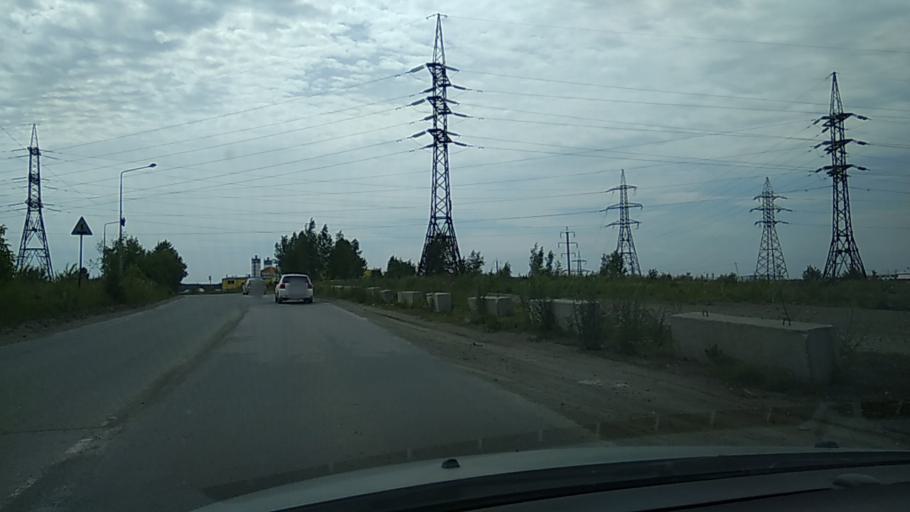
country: RU
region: Sverdlovsk
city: Verkhnyaya Pyshma
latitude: 56.9559
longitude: 60.5879
